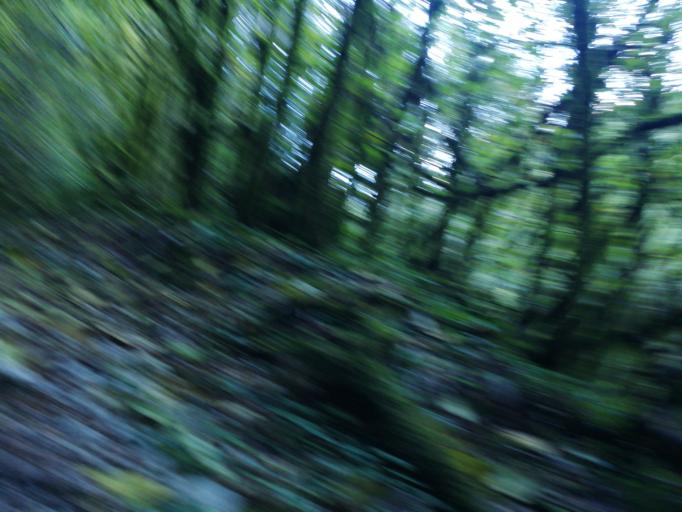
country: GE
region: Abkhazia
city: Gagra
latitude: 43.3255
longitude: 40.2556
